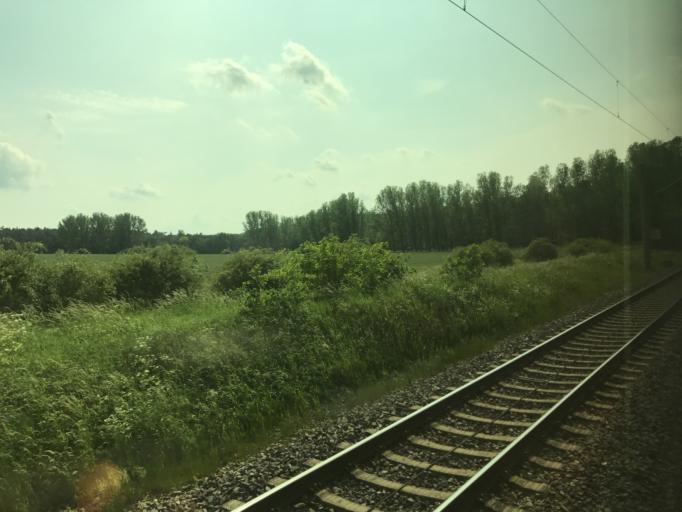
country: DE
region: Brandenburg
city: Nennhausen
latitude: 52.6006
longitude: 12.4892
